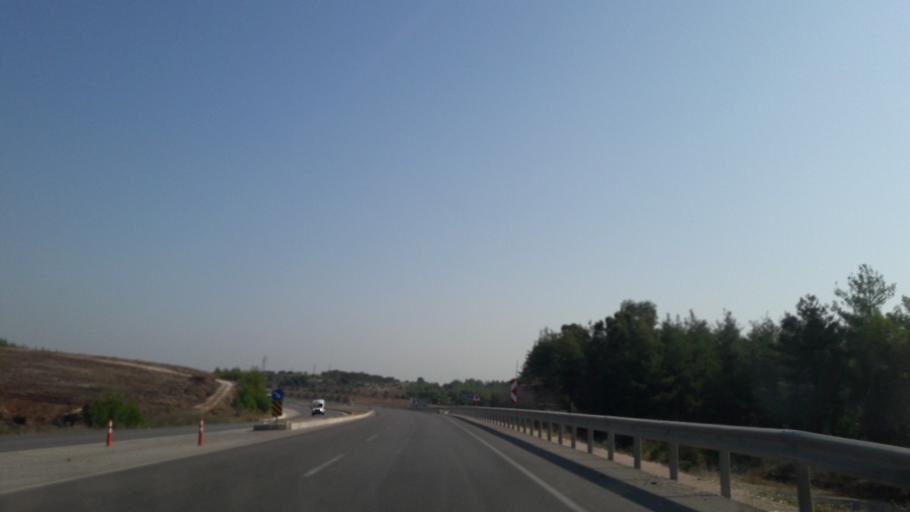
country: TR
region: Adana
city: Sagkaya
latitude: 37.1585
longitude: 35.5528
